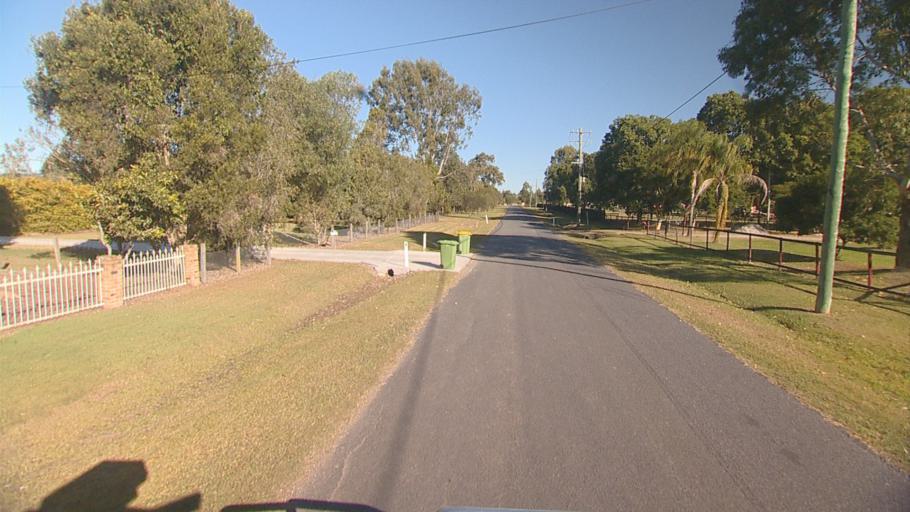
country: AU
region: Queensland
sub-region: Logan
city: Logan Reserve
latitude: -27.7400
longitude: 153.1132
